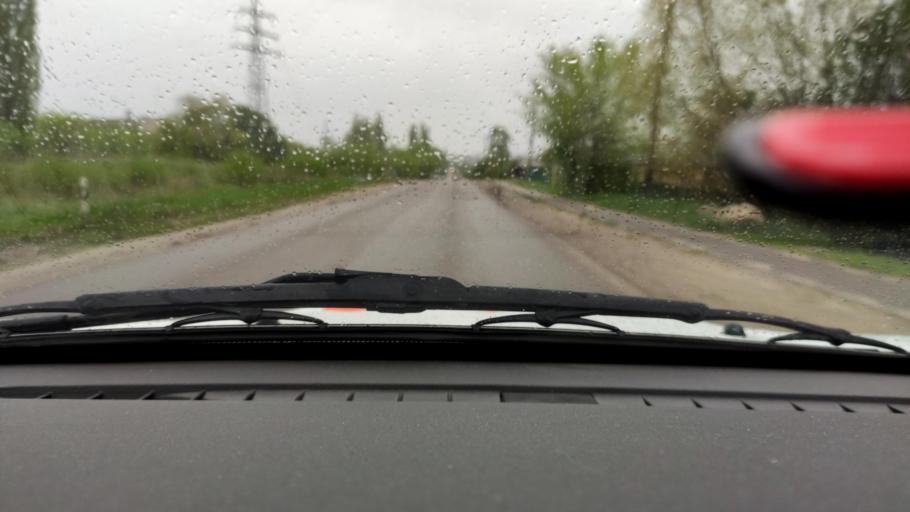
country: RU
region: Voronezj
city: Strelitsa
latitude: 51.6214
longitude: 38.9109
